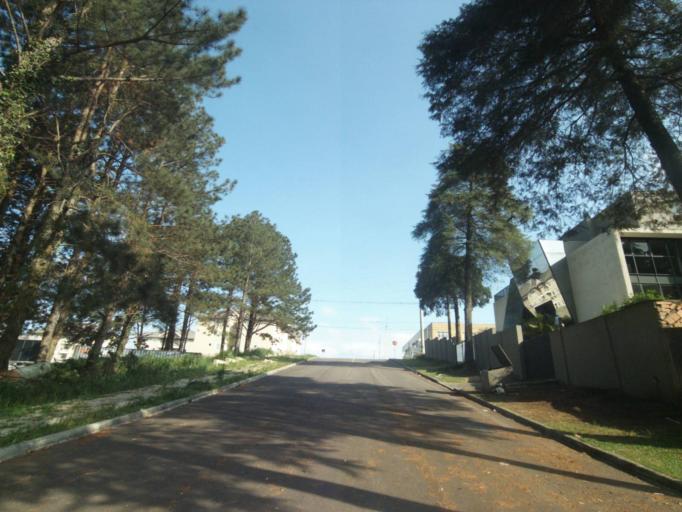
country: BR
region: Parana
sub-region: Pinhais
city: Pinhais
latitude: -25.4086
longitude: -49.2159
